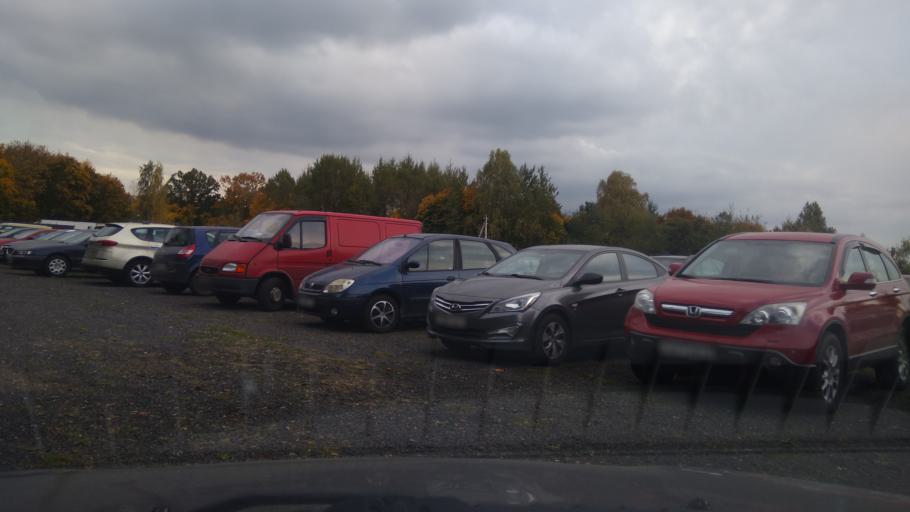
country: BY
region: Minsk
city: Dukora
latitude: 53.6771
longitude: 27.9624
